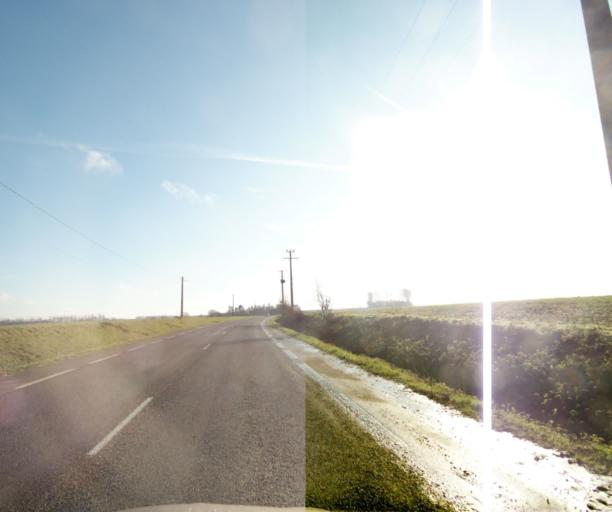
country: FR
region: Nord-Pas-de-Calais
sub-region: Departement du Nord
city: Saultain
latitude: 50.3262
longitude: 3.5616
